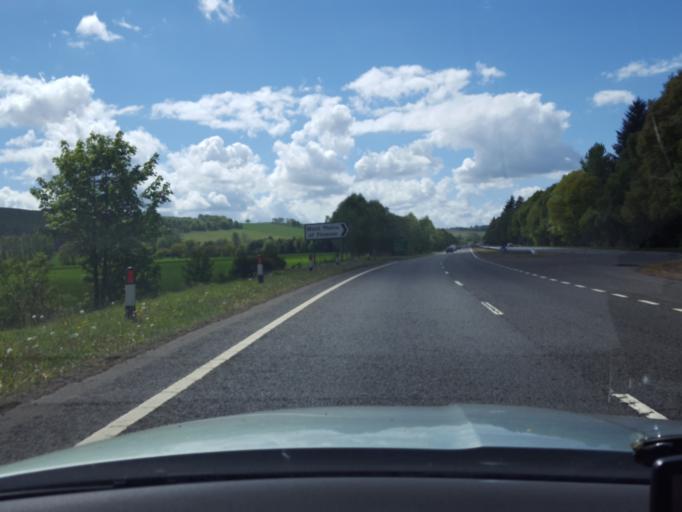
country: GB
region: Scotland
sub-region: Angus
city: Forfar
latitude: 56.6957
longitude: -2.8347
